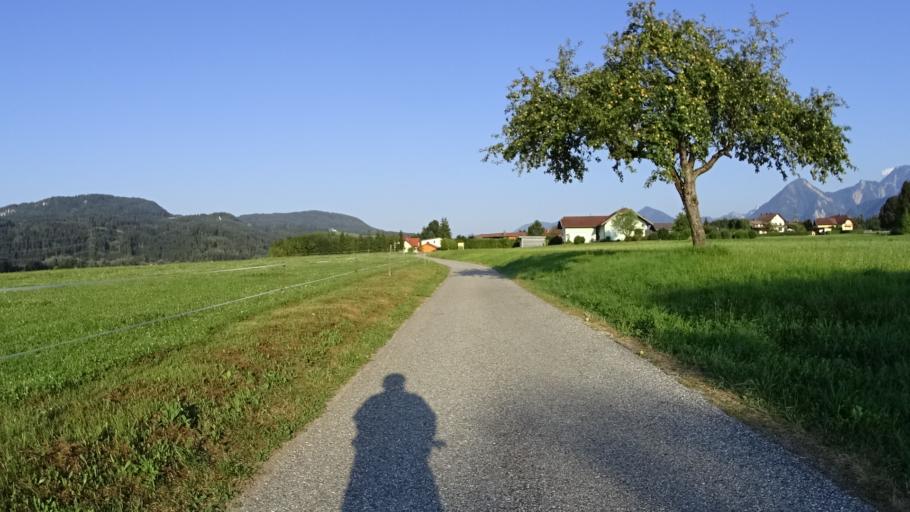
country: AT
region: Carinthia
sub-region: Politischer Bezirk Villach Land
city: Sankt Jakob
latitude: 46.5538
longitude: 14.0603
